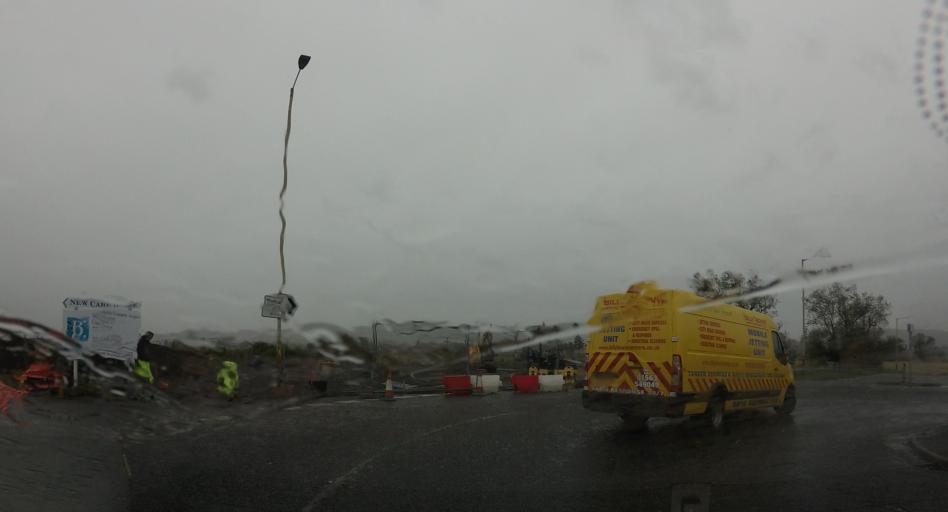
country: GB
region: Scotland
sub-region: Perth and Kinross
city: Coupar Angus
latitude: 56.5464
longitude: -3.2635
